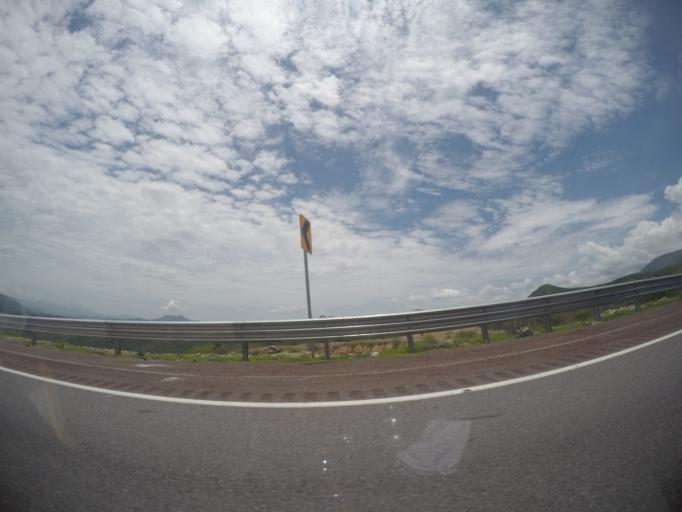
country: MX
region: Guerrero
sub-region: Huitzuco de los Figueroa
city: San Francisco Ozomatlan
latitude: 17.9479
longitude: -99.3684
